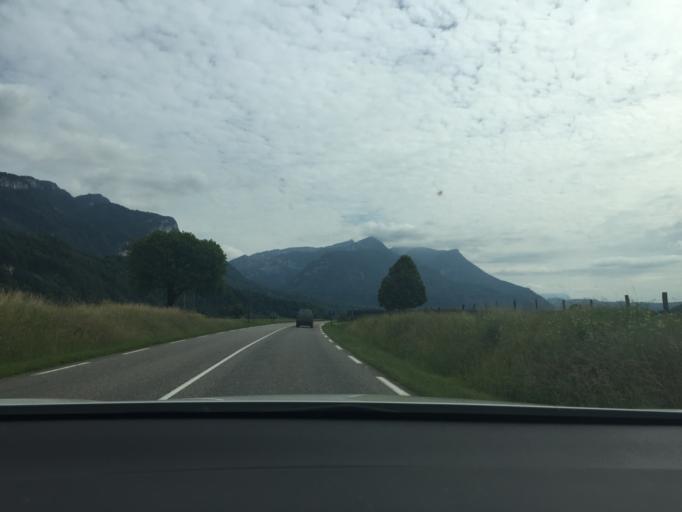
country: FR
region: Rhone-Alpes
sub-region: Departement de la Savoie
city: Les Echelles
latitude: 45.4334
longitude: 5.7653
